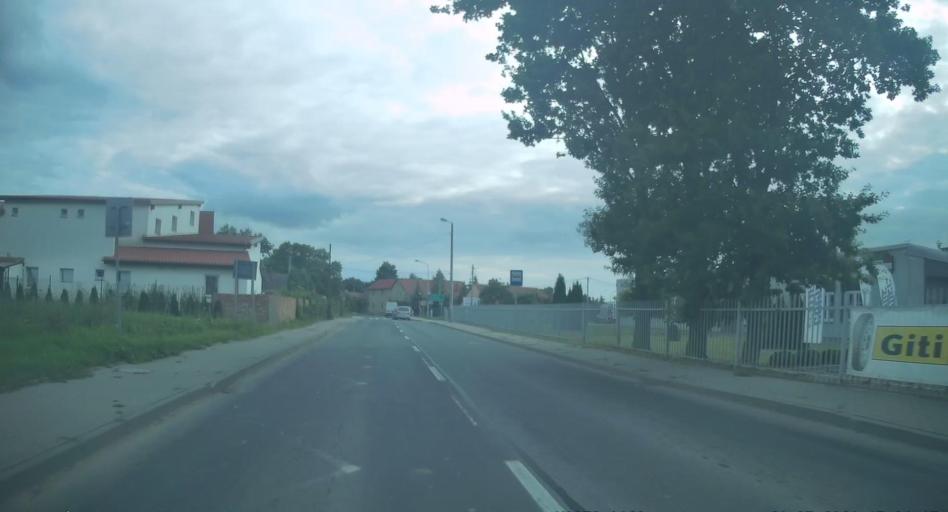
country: PL
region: Lower Silesian Voivodeship
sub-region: Powiat wroclawski
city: Gniechowice
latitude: 51.0133
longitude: 16.8729
